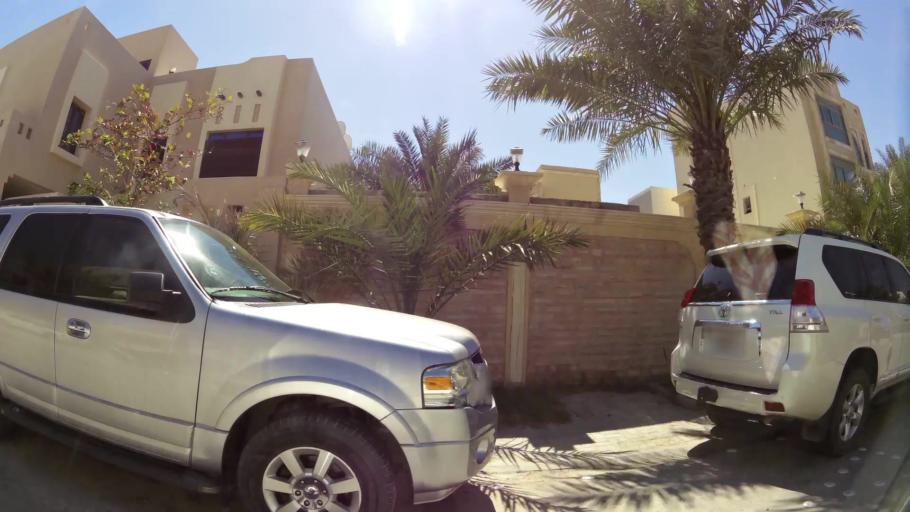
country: BH
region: Muharraq
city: Al Muharraq
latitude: 26.2807
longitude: 50.6409
